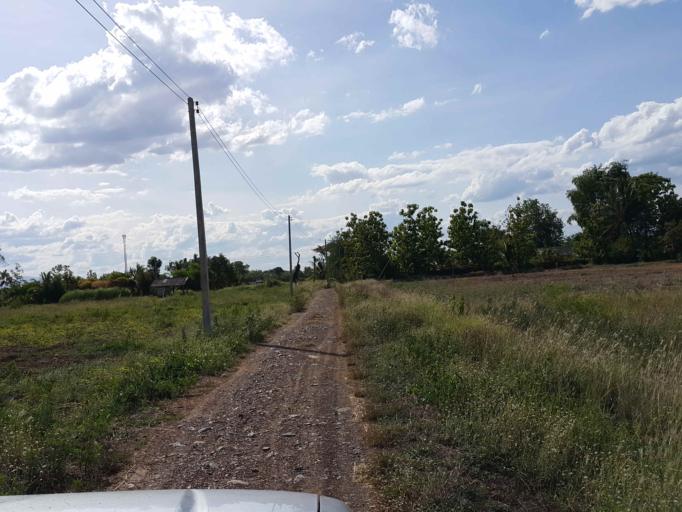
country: TH
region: Chiang Mai
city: San Kamphaeng
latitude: 18.8002
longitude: 99.1524
